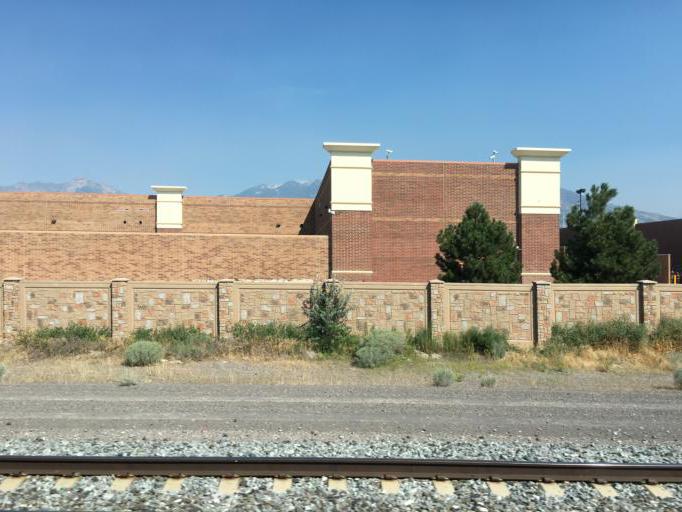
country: US
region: Utah
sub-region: Salt Lake County
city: South Jordan
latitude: 40.5471
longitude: -111.9026
